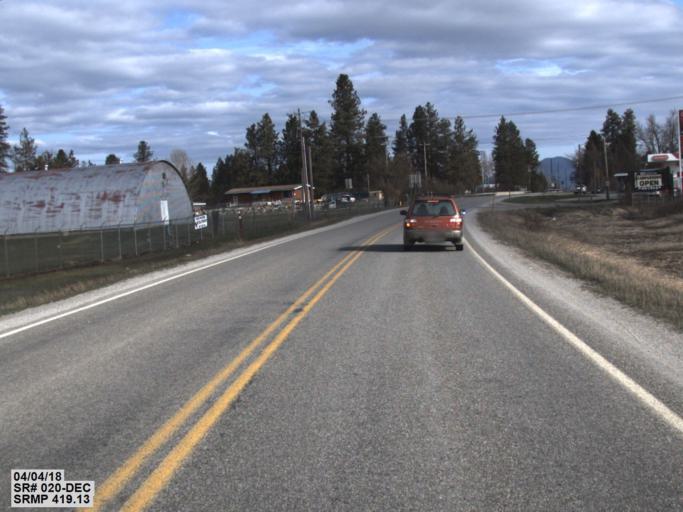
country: US
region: Washington
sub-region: Pend Oreille County
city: Newport
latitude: 48.3356
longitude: -117.3040
